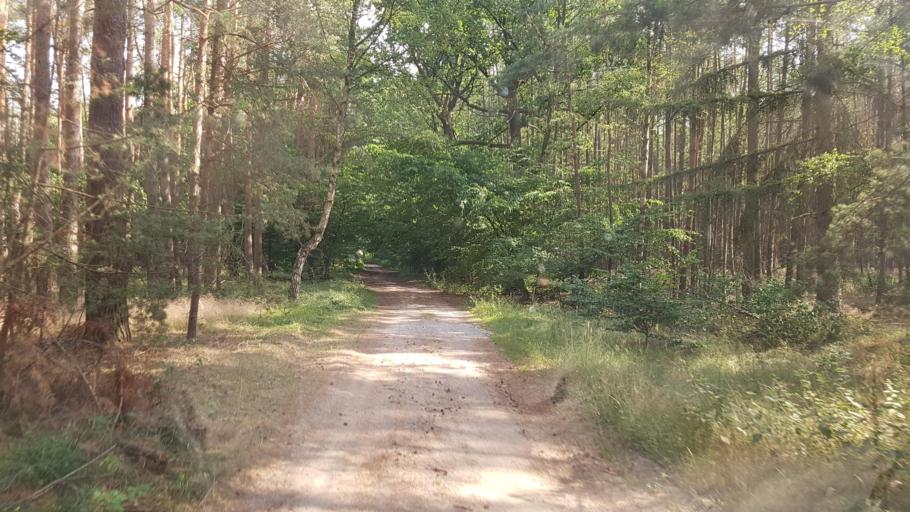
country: DE
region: Brandenburg
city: Belzig
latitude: 52.1870
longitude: 12.6052
